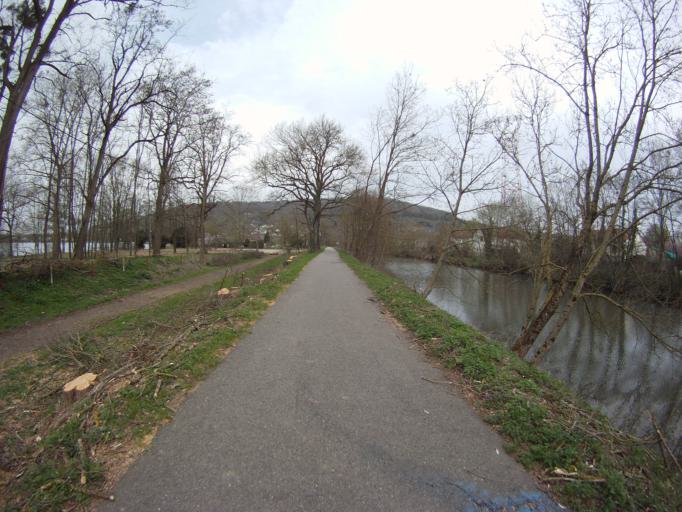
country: FR
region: Lorraine
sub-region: Departement de Meurthe-et-Moselle
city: Messein
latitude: 48.6068
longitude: 6.1497
